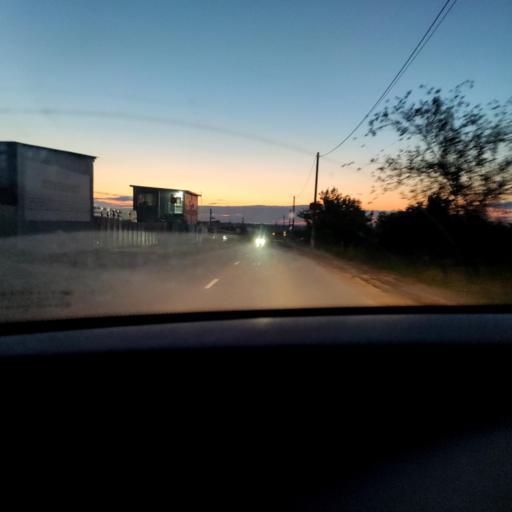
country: RU
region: Samara
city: Novosemeykino
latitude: 53.4015
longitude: 50.3225
